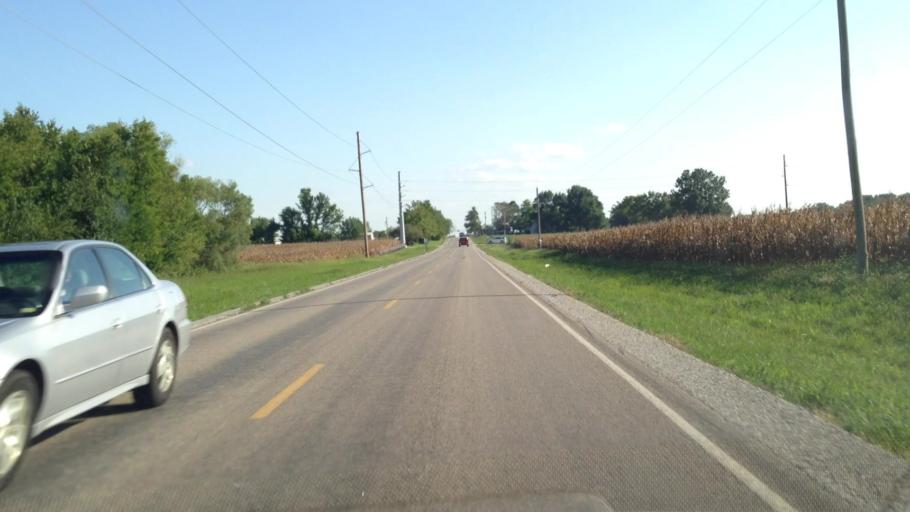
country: US
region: Kansas
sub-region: Crawford County
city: Pittsburg
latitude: 37.3695
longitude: -94.6314
